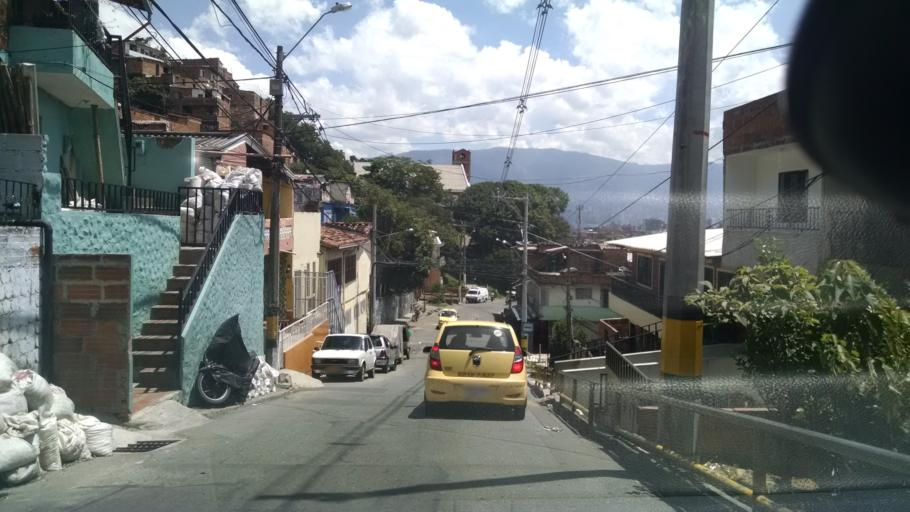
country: CO
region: Antioquia
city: Medellin
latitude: 6.2621
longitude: -75.6129
